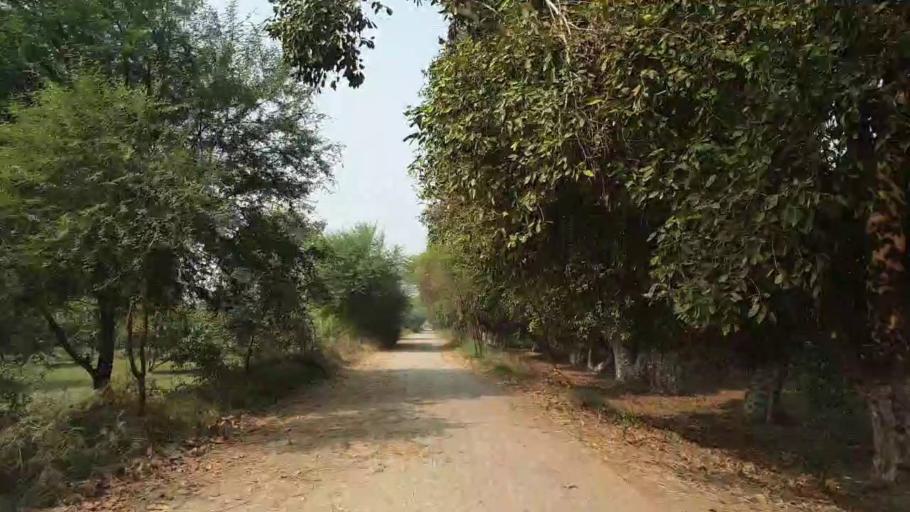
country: PK
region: Sindh
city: Tando Muhammad Khan
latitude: 25.2170
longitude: 68.5549
